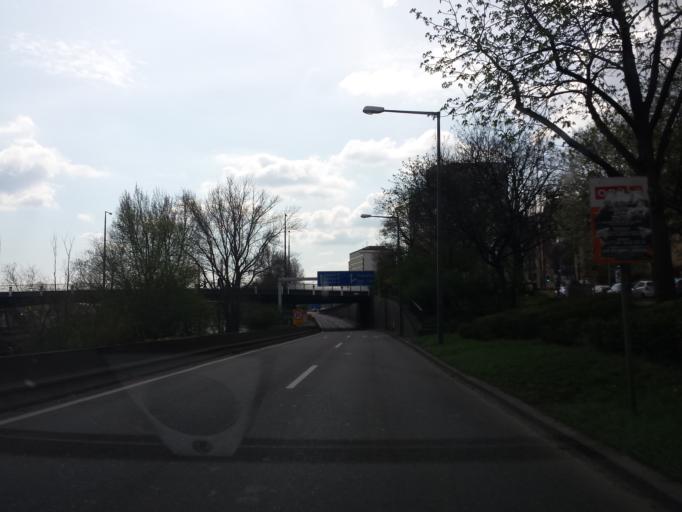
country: AT
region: Vienna
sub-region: Wien Stadt
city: Vienna
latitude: 48.1973
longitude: 16.4094
